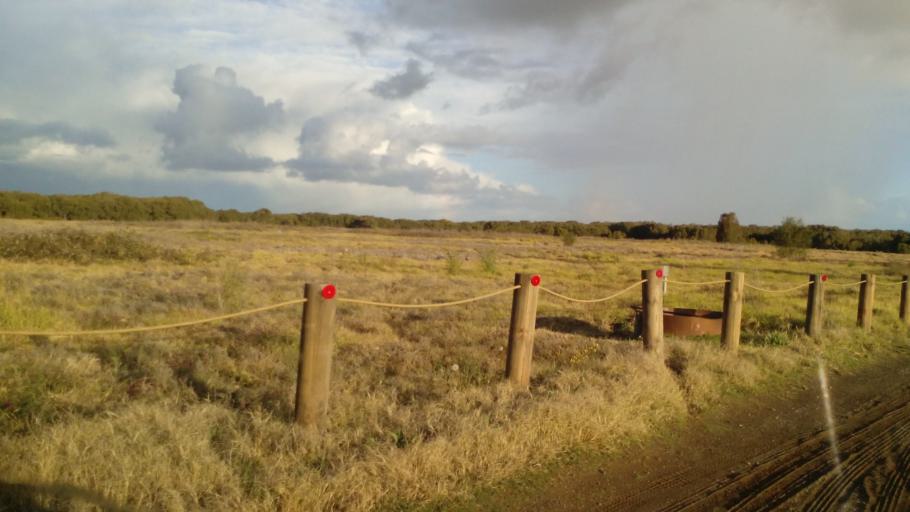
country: AU
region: New South Wales
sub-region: Newcastle
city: Mayfield West
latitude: -32.8417
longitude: 151.7174
